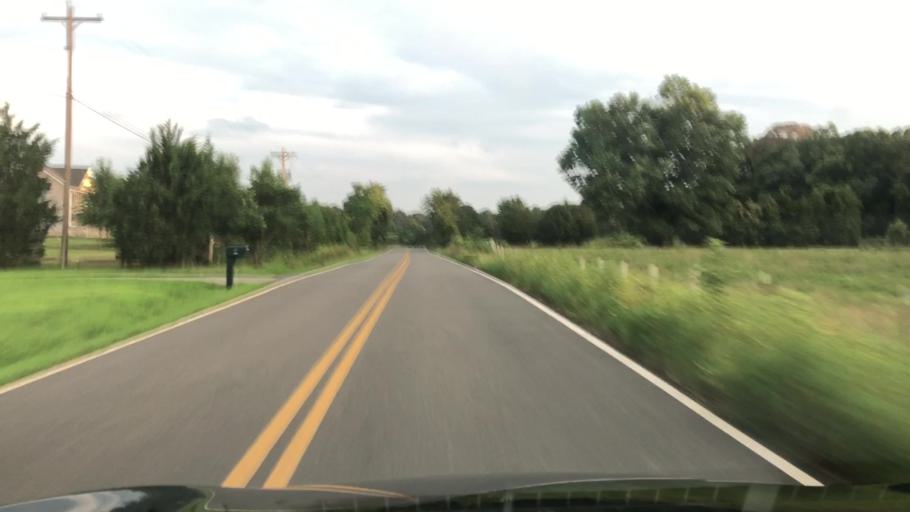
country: US
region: Virginia
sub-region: Fauquier County
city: Bealeton
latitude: 38.5496
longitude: -77.6760
